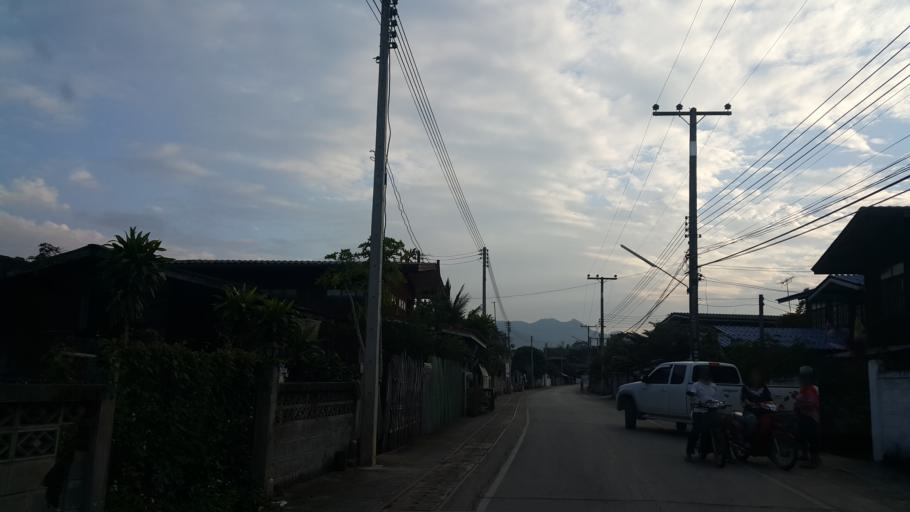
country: TH
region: Lampang
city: Sop Prap
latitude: 17.8649
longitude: 99.3299
